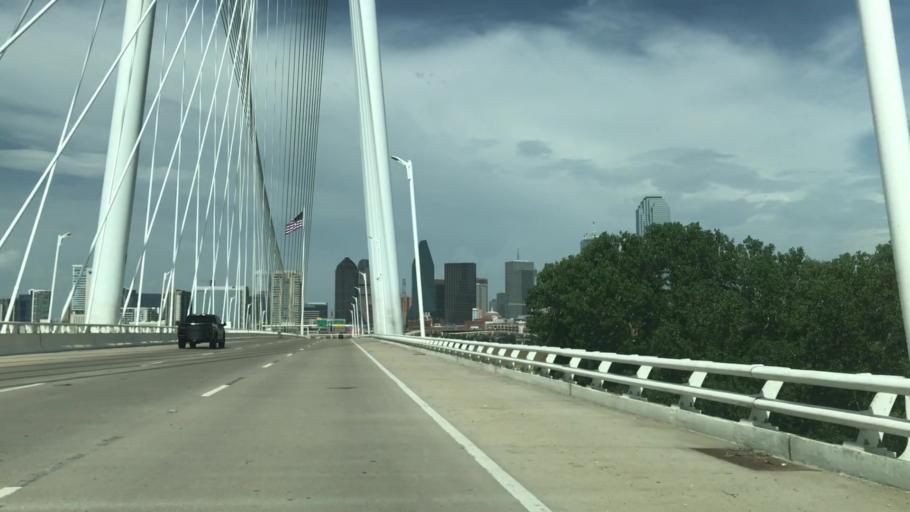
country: US
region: Texas
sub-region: Dallas County
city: Dallas
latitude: 32.7795
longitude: -96.8233
